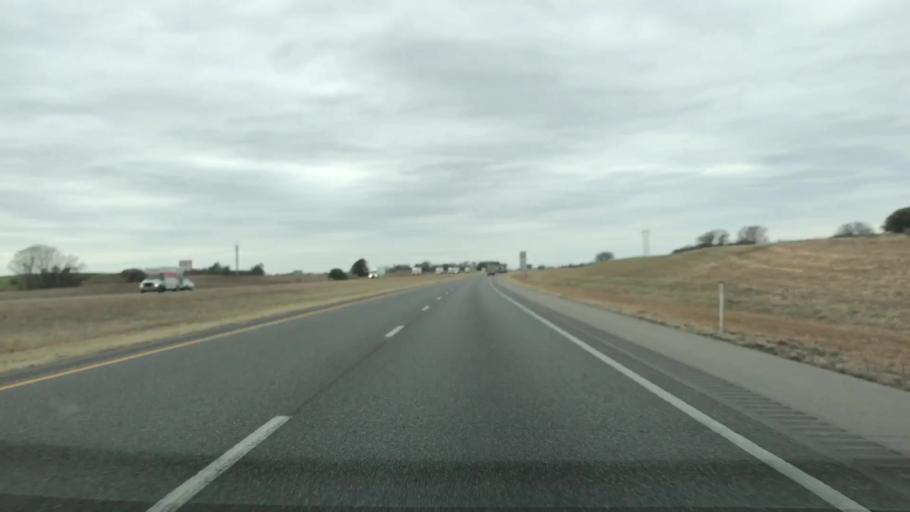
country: US
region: Oklahoma
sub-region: Beckham County
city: Erick
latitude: 35.2273
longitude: -99.9225
